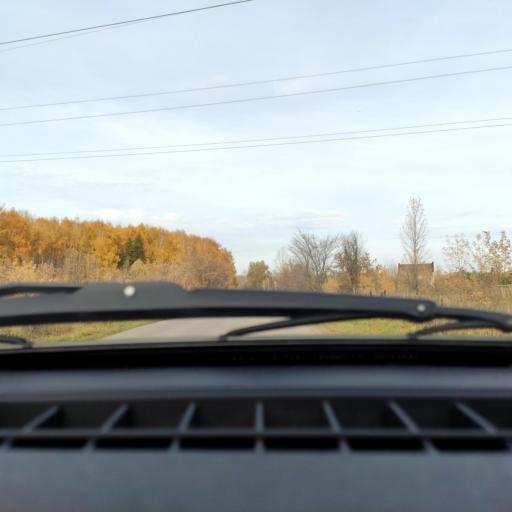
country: RU
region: Bashkortostan
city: Ufa
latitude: 54.7870
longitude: 56.1602
